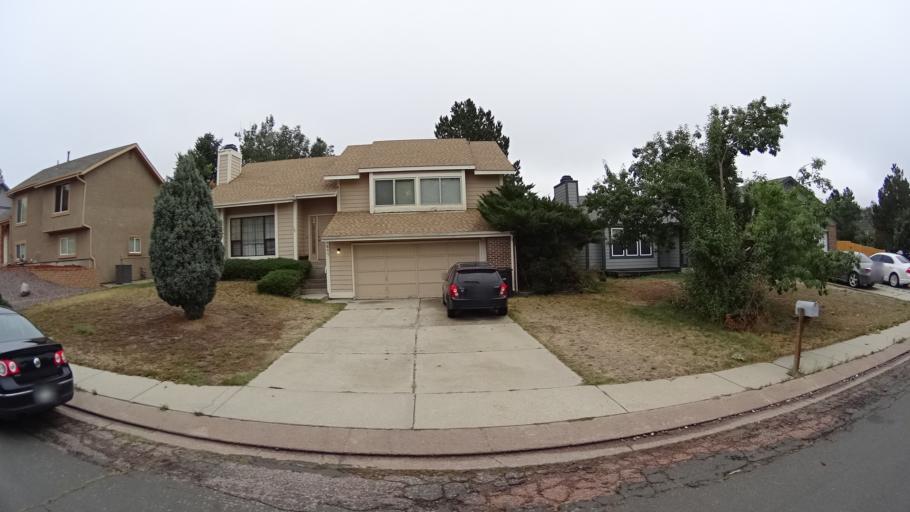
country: US
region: Colorado
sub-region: El Paso County
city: Cimarron Hills
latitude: 38.9318
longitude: -104.7686
